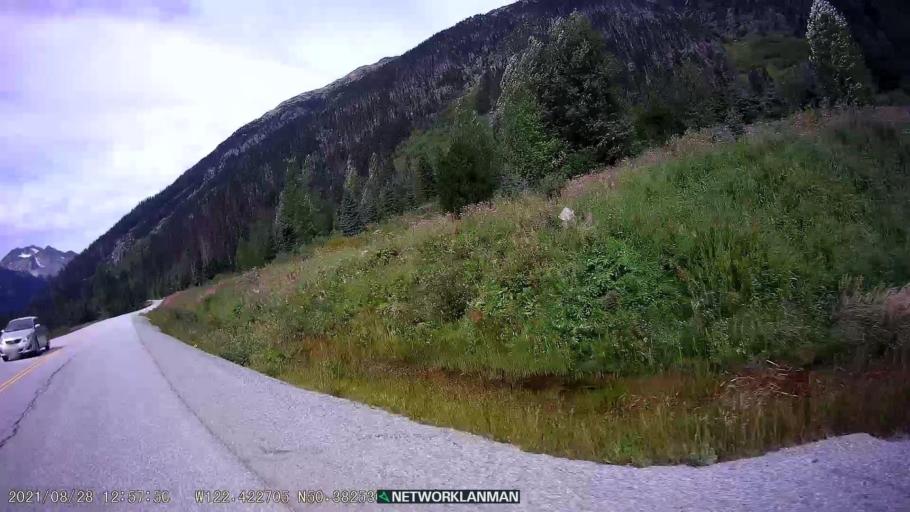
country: CA
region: British Columbia
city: Pemberton
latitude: 50.3808
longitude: -122.4198
